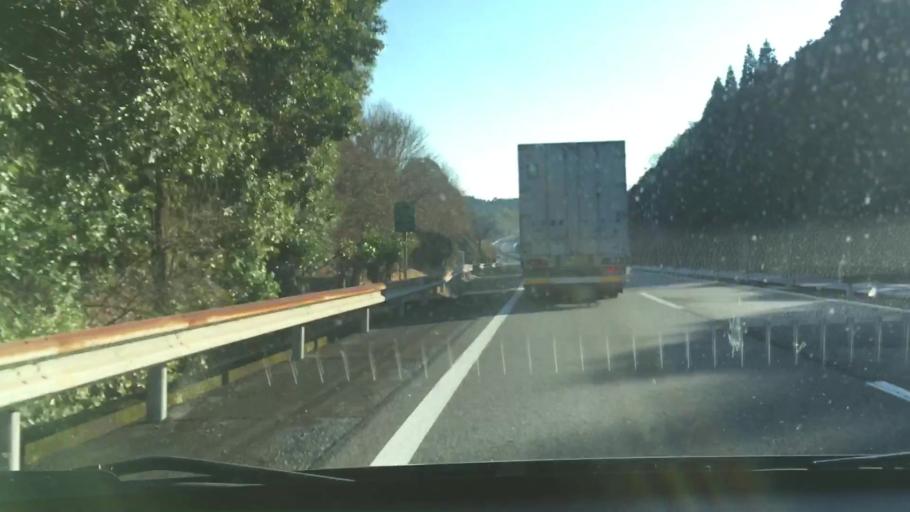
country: JP
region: Kagoshima
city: Kajiki
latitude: 31.8847
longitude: 130.6956
